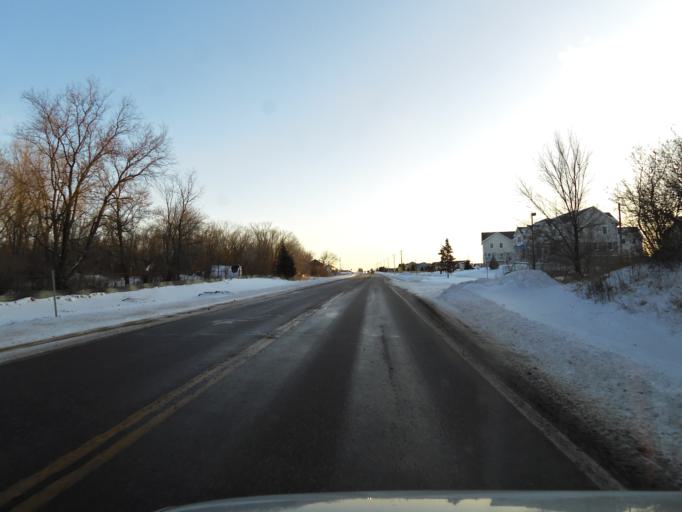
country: US
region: Minnesota
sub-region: Washington County
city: Lake Elmo
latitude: 44.9407
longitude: -92.8832
